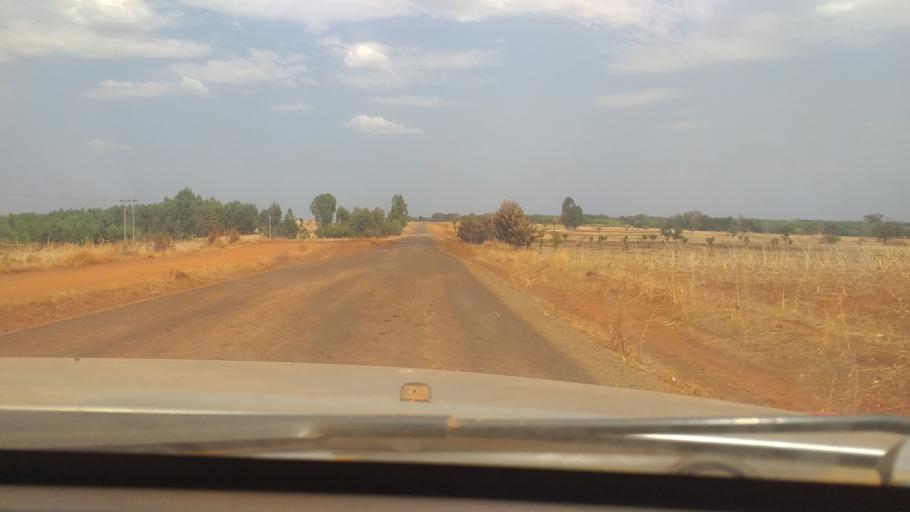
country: ET
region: Binshangul Gumuz
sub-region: Asosa
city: Asosa
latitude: 10.0790
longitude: 34.6458
